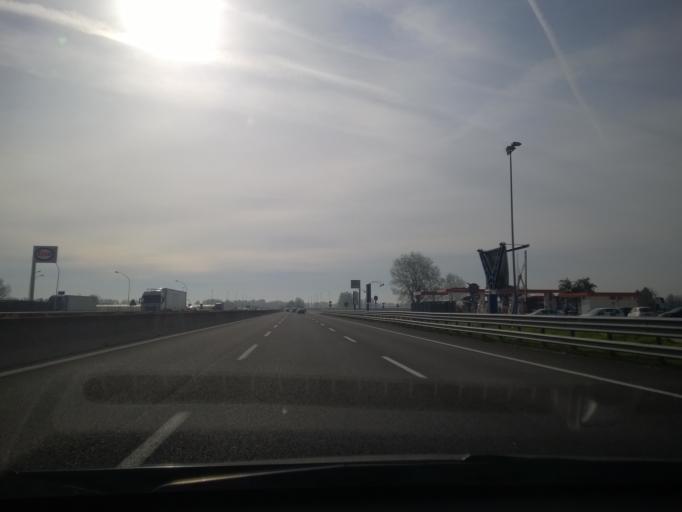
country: IT
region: Emilia-Romagna
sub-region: Provincia di Ravenna
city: Solarolo
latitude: 44.3425
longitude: 11.8472
